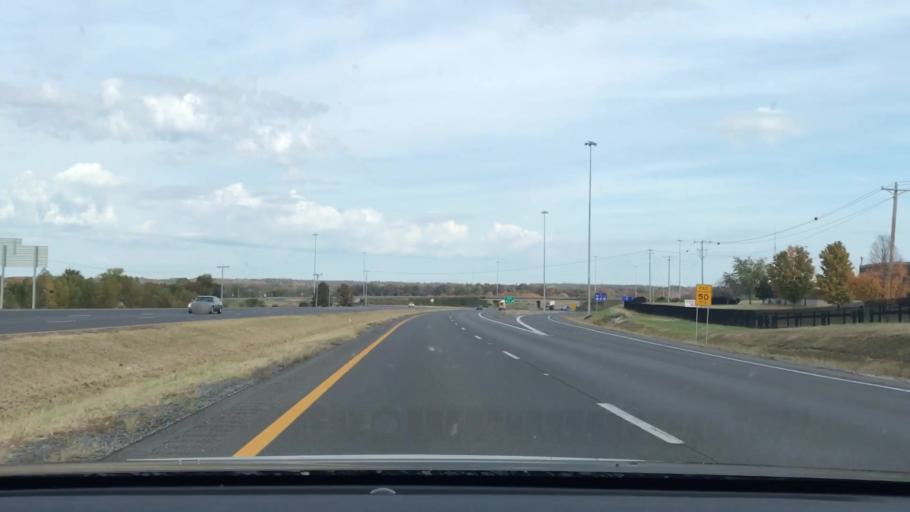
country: US
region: Kentucky
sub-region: Marshall County
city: Benton
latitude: 36.8641
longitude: -88.3667
